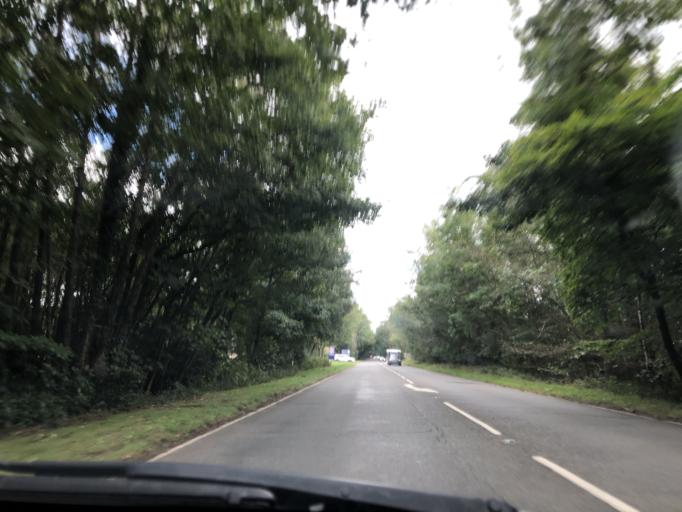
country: GB
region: England
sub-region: East Sussex
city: Forest Row
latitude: 51.0653
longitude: 0.0280
